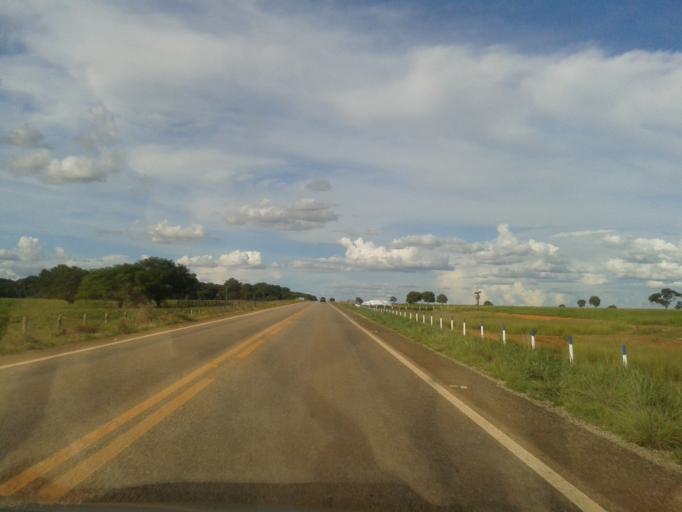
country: BR
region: Goias
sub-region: Mozarlandia
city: Mozarlandia
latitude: -14.3376
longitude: -50.4169
